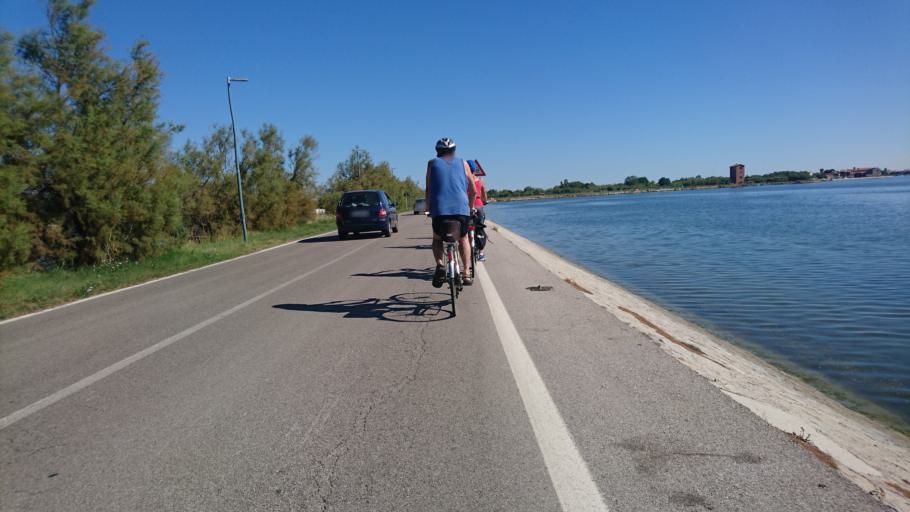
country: IT
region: Veneto
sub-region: Provincia di Venezia
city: San Pietro in Volta
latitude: 45.3307
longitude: 12.3200
